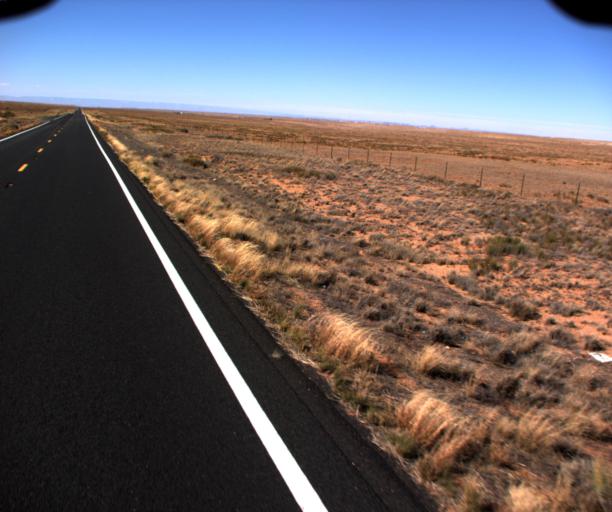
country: US
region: Arizona
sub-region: Coconino County
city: Tuba City
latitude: 36.0140
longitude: -111.0863
